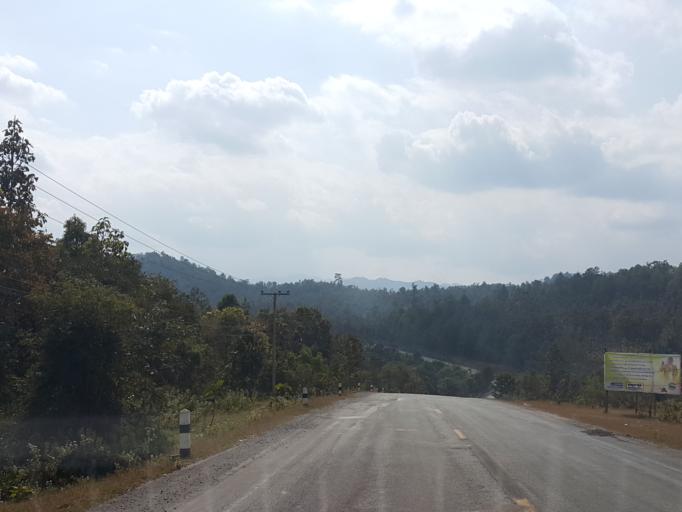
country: TH
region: Chiang Mai
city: Om Koi
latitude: 17.8276
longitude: 98.3627
